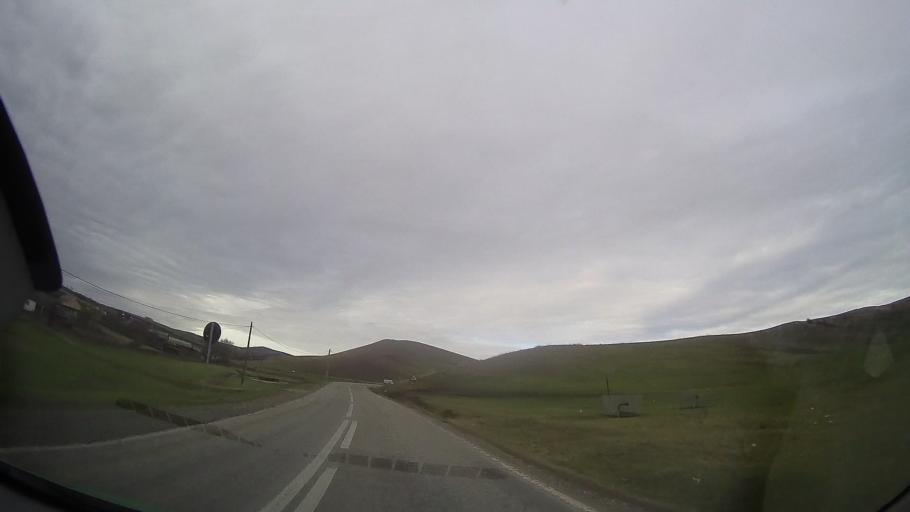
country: RO
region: Cluj
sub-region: Comuna Camarasu
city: Camarasu
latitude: 46.7963
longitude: 24.1753
